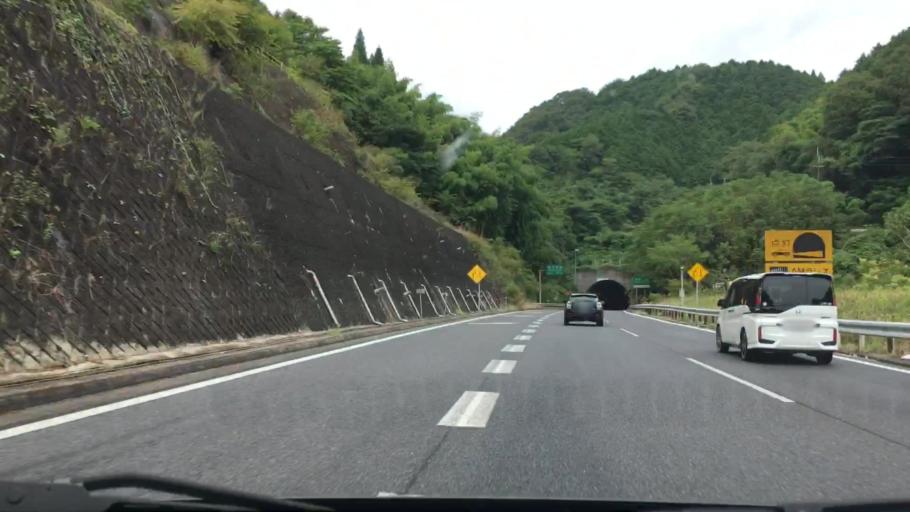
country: JP
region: Okayama
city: Tsuyama
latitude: 35.0144
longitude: 134.2692
